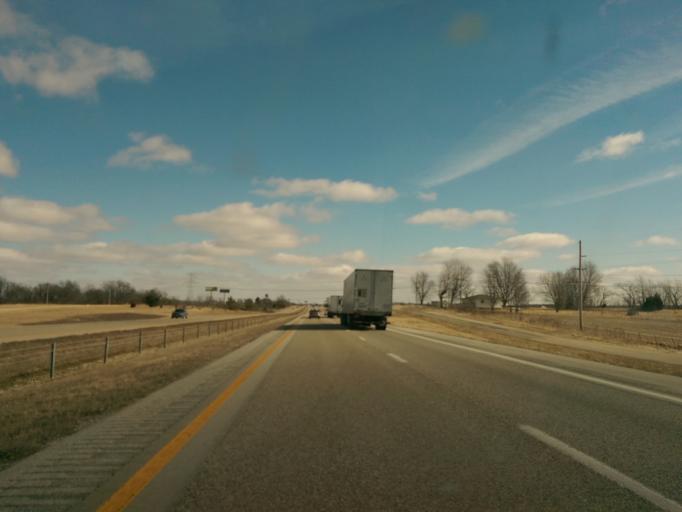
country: US
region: Missouri
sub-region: Montgomery County
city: Montgomery City
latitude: 38.9043
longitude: -91.4932
